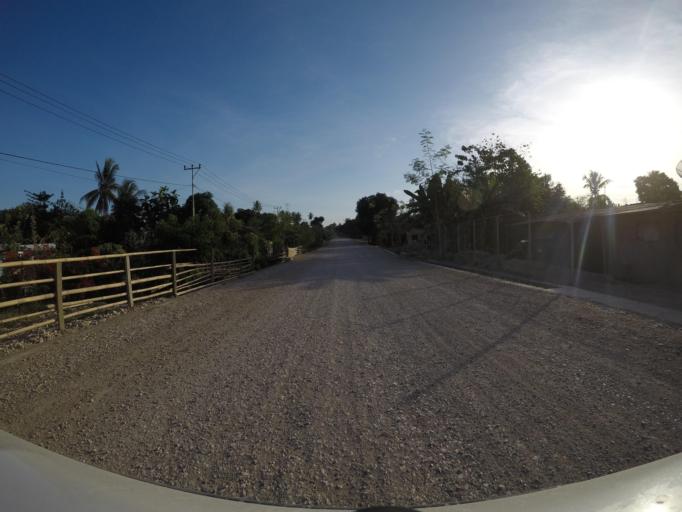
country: TL
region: Viqueque
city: Viqueque
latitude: -8.8227
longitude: 126.5318
